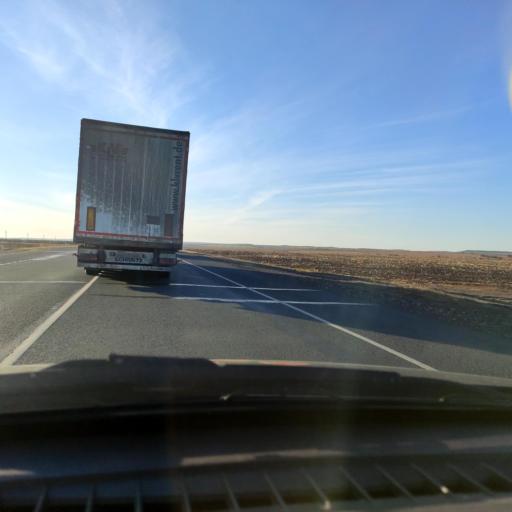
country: RU
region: Samara
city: Balasheyka
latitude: 53.1909
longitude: 48.1394
